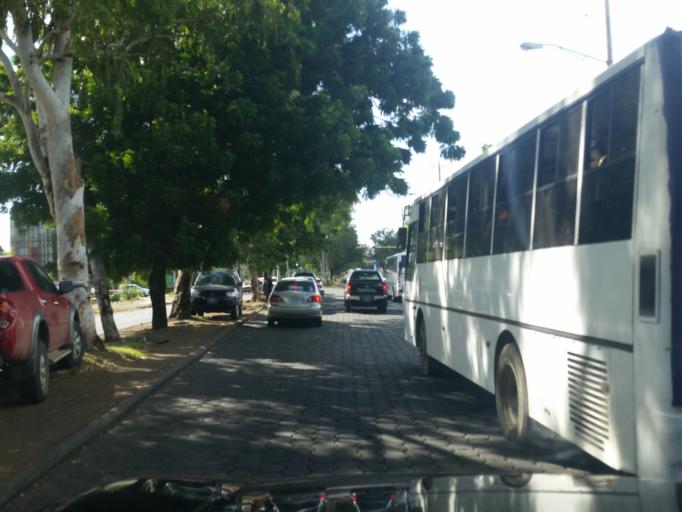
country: NI
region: Managua
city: Managua
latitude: 12.1291
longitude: -86.2450
